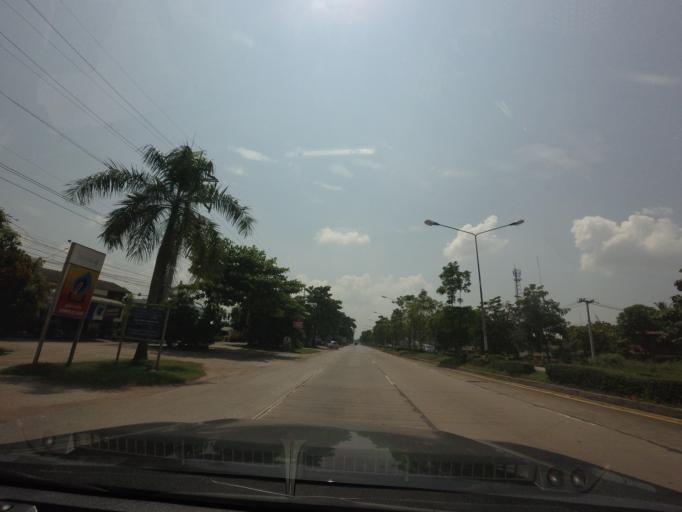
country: TH
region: Uttaradit
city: Uttaradit
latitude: 17.6191
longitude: 100.1243
